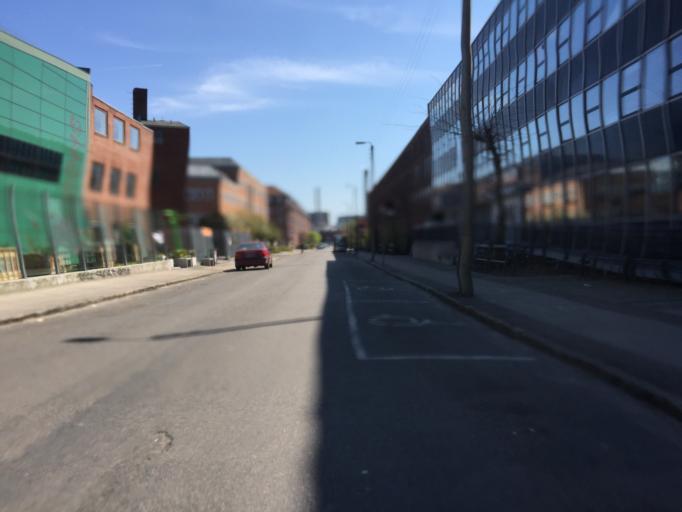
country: DK
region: Capital Region
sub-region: Frederiksberg Kommune
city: Frederiksberg
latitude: 55.7007
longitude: 12.5292
